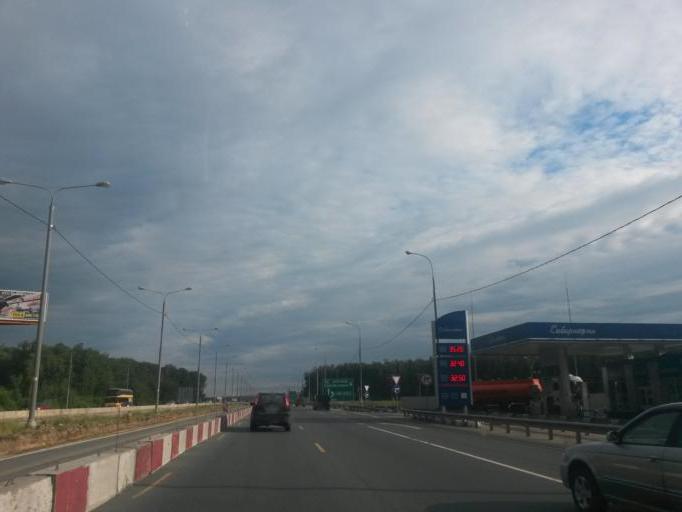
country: RU
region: Moskovskaya
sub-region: Podol'skiy Rayon
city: Podol'sk
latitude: 55.3995
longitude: 37.6049
